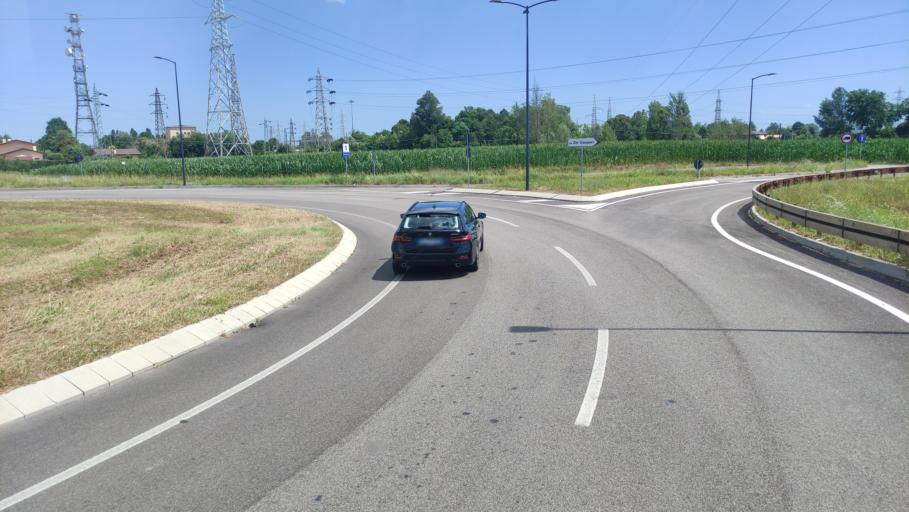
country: IT
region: Veneto
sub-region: Provincia di Venezia
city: Scorze
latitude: 45.5609
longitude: 12.1082
